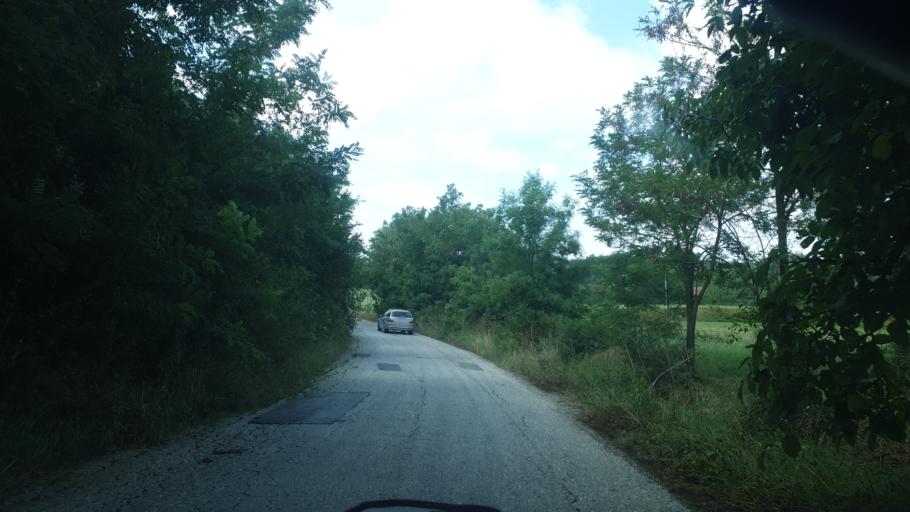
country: RS
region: Central Serbia
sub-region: Sumadijski Okrug
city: Kragujevac
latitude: 44.1026
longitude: 20.7809
